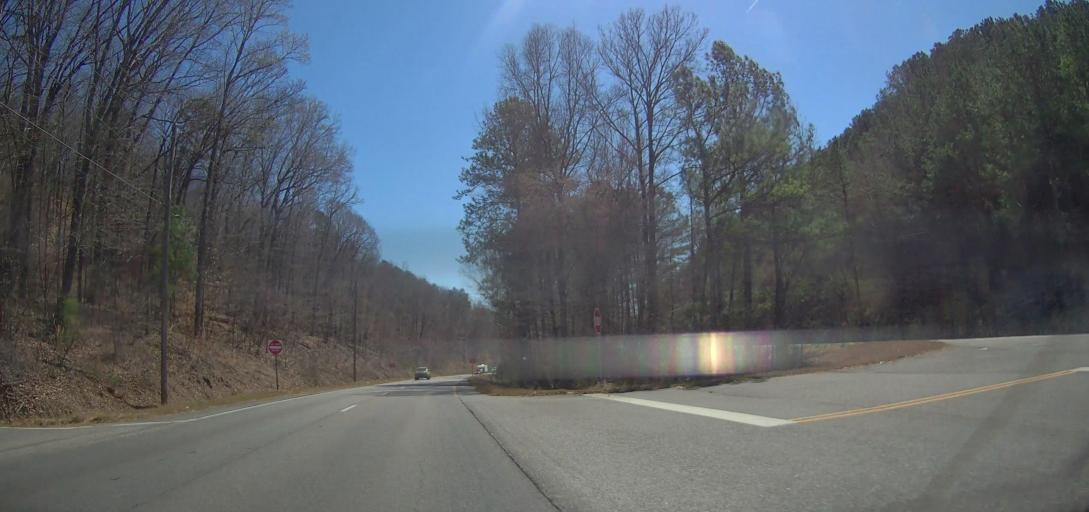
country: US
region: Alabama
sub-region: Etowah County
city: Rainbow City
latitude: 33.9485
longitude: -86.0304
